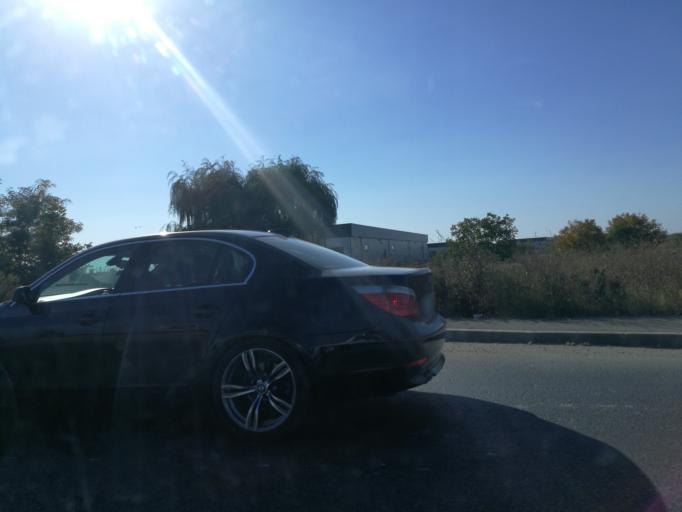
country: RO
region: Ilfov
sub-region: Comuna Chiajna
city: Chiajna
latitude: 44.4527
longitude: 25.9615
